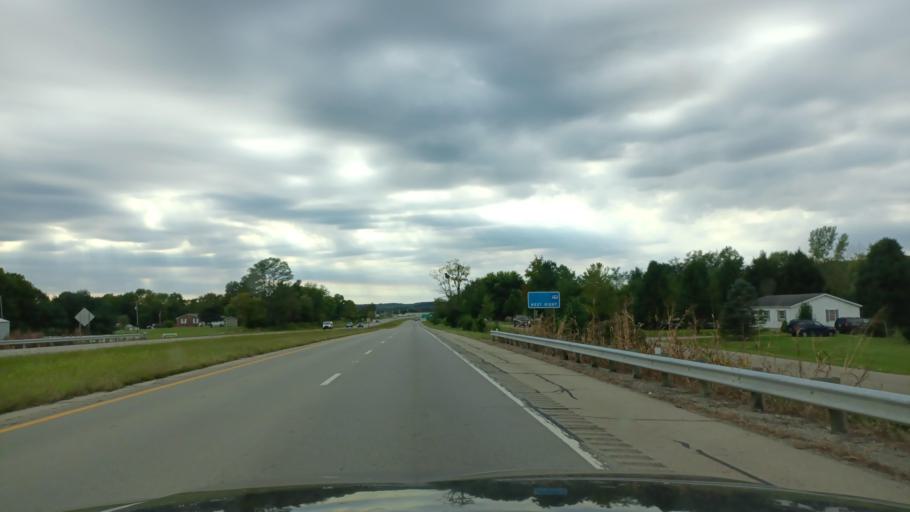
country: US
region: Ohio
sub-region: Ross County
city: North Fork Village
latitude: 39.3742
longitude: -83.0430
